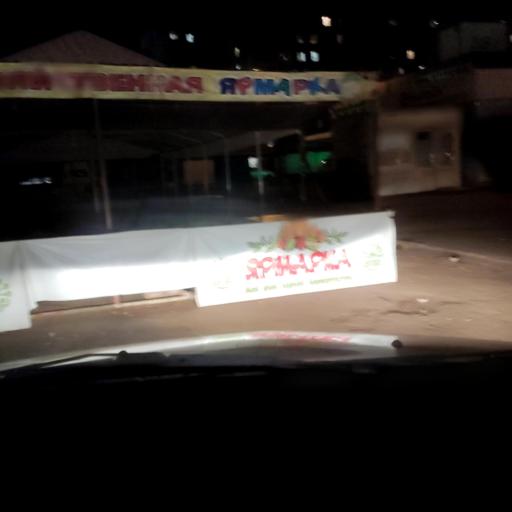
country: RU
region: Bashkortostan
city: Ufa
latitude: 54.7024
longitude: 56.0025
